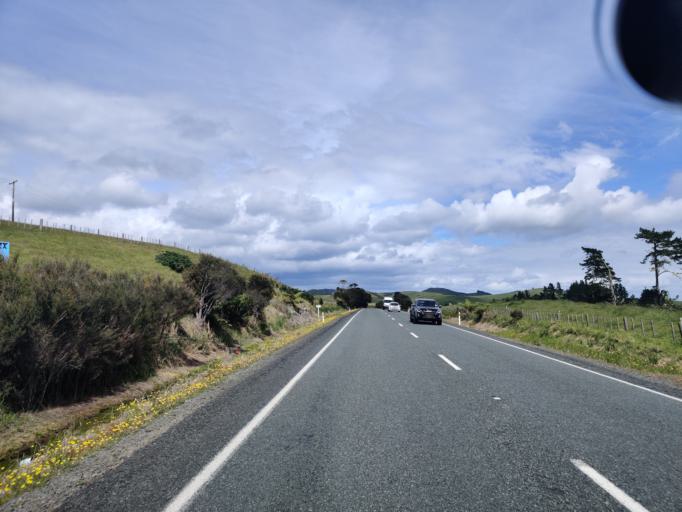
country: NZ
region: Northland
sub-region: Far North District
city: Taipa
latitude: -35.0438
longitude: 173.6630
